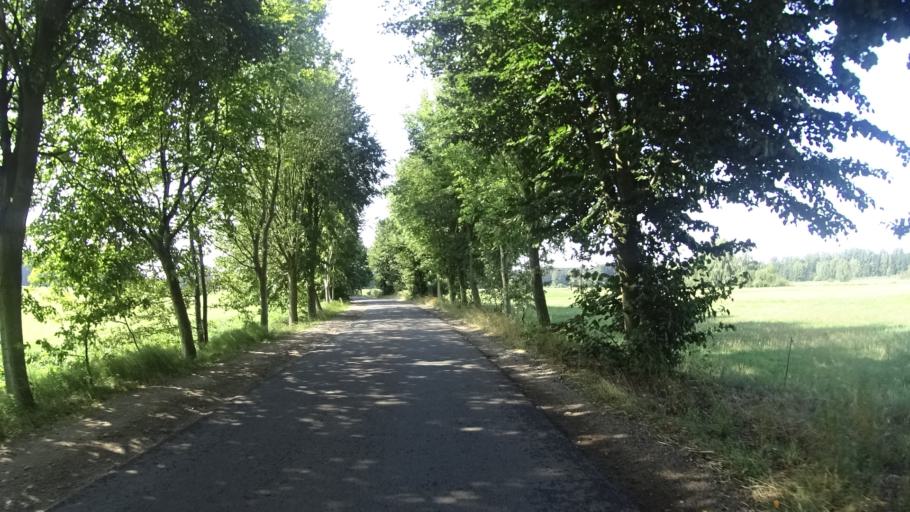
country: DE
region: Brandenburg
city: Straupitz
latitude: 51.8859
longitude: 14.1253
